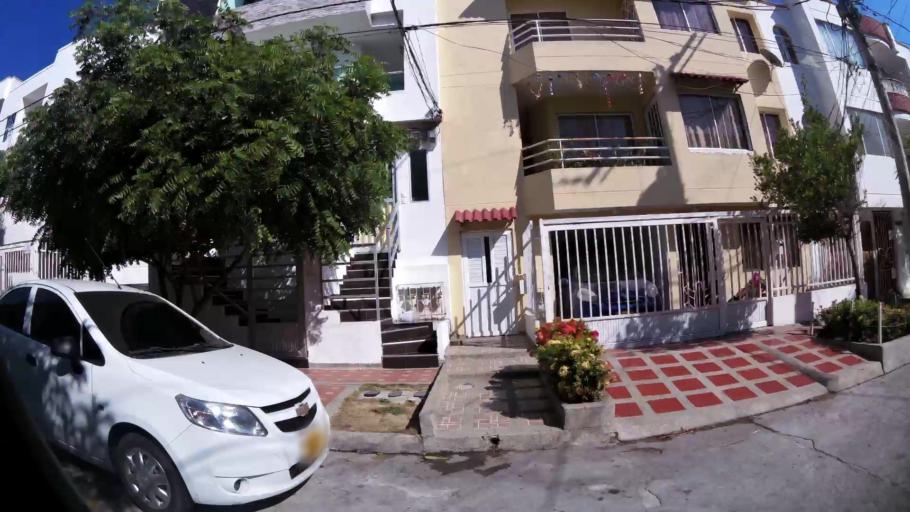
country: CO
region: Atlantico
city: Barranquilla
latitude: 11.0239
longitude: -74.8118
